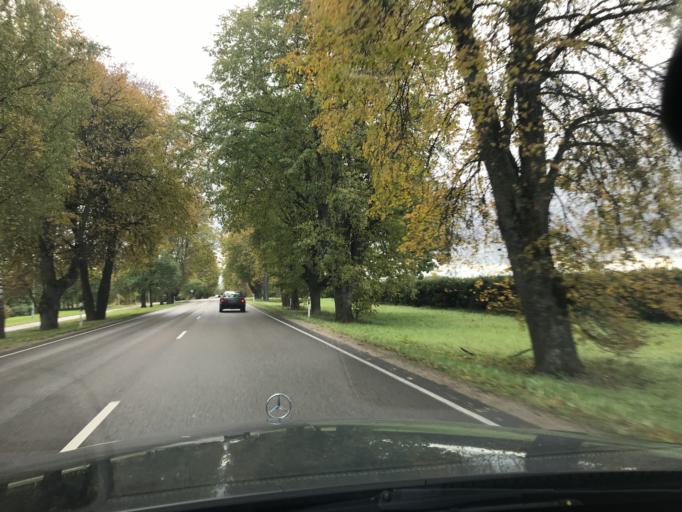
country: EE
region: Valgamaa
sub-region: Torva linn
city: Torva
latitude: 58.0132
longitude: 25.8856
